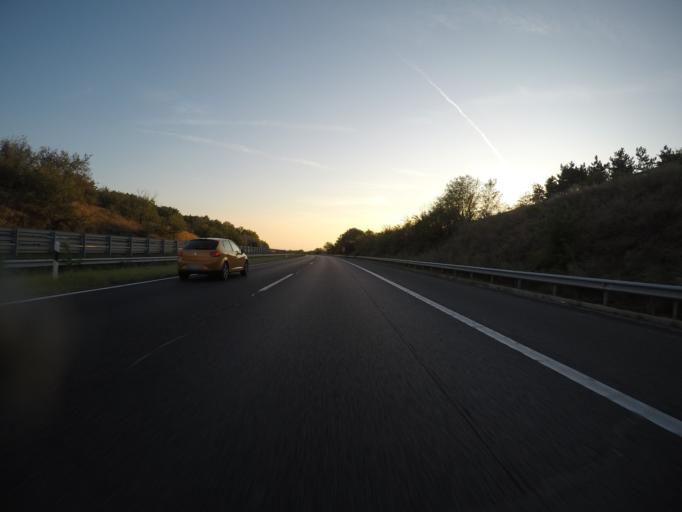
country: HU
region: Fejer
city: Pakozd
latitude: 47.2315
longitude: 18.5826
